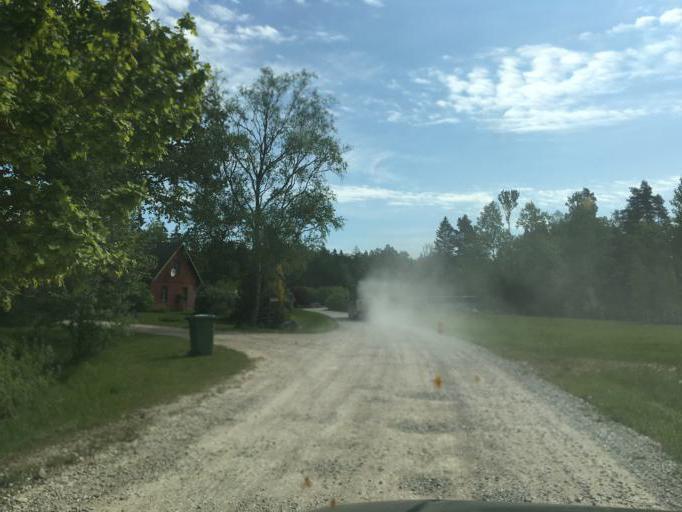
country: LV
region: Talsu Rajons
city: Valdemarpils
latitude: 57.3718
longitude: 22.5246
